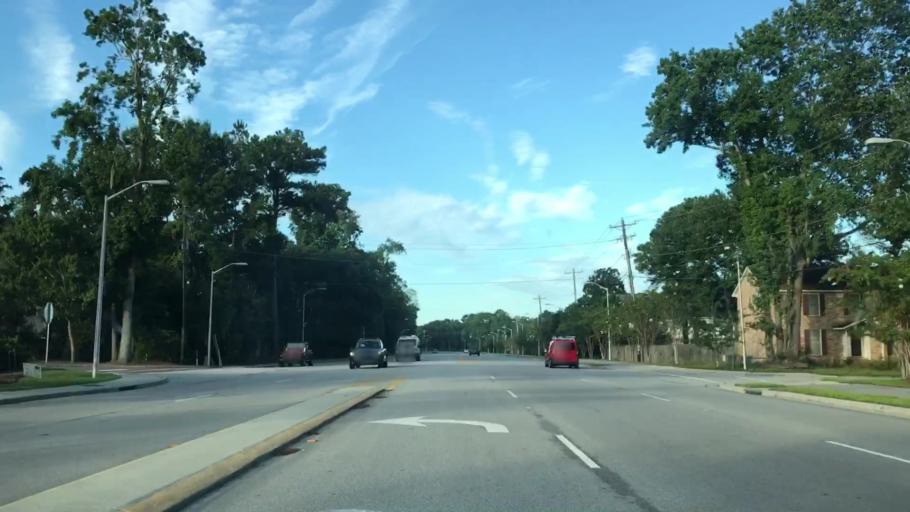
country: US
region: South Carolina
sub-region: Charleston County
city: Shell Point
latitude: 32.8431
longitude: -80.0603
